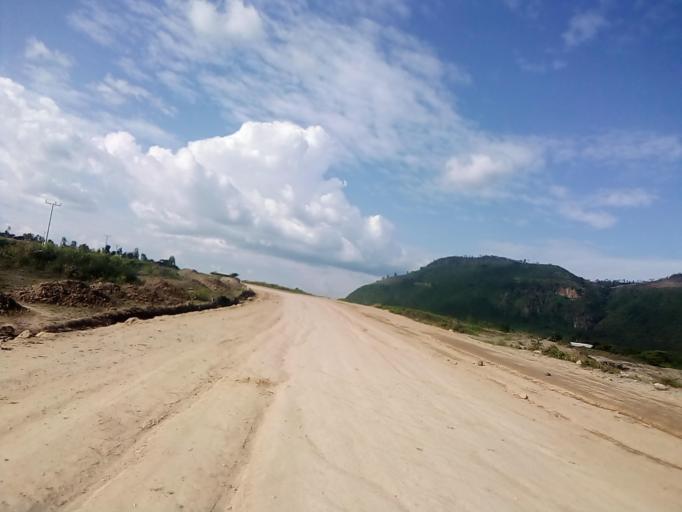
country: ET
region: Southern Nations, Nationalities, and People's Region
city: K'olito
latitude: 7.6273
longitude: 38.0636
